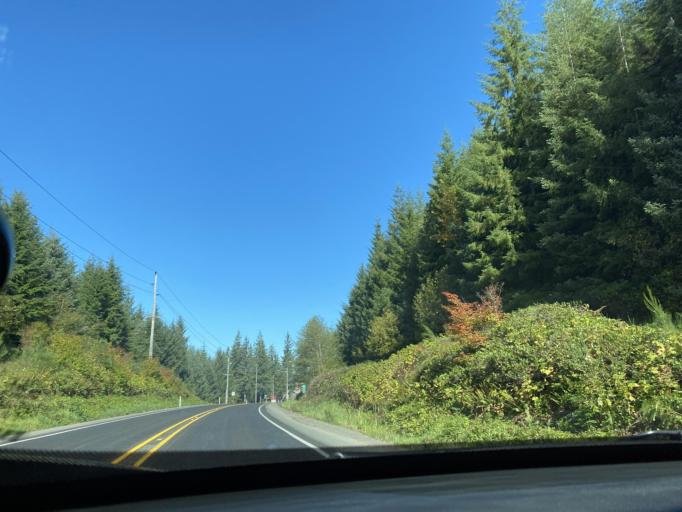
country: US
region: Washington
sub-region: Clallam County
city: Forks
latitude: 47.9651
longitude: -124.4021
